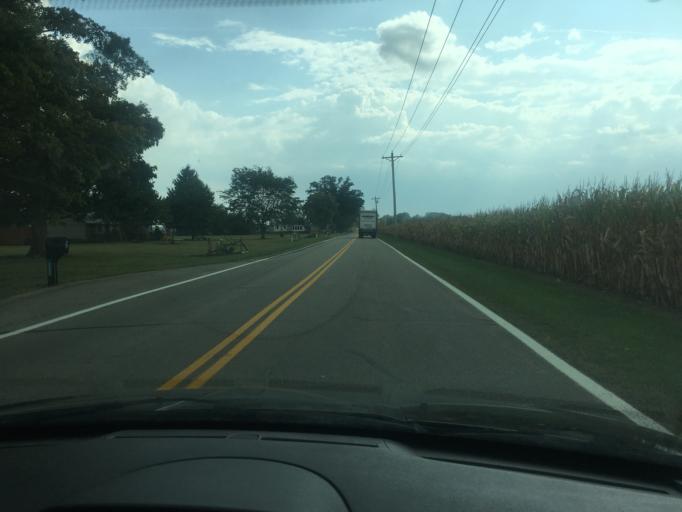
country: US
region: Ohio
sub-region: Champaign County
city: Urbana
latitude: 40.1591
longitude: -83.8137
